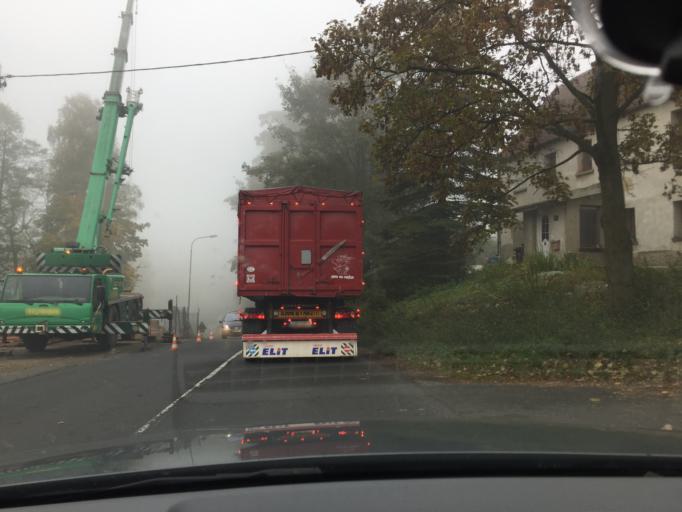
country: CZ
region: Ustecky
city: Libouchec
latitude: 50.7803
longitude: 14.0335
